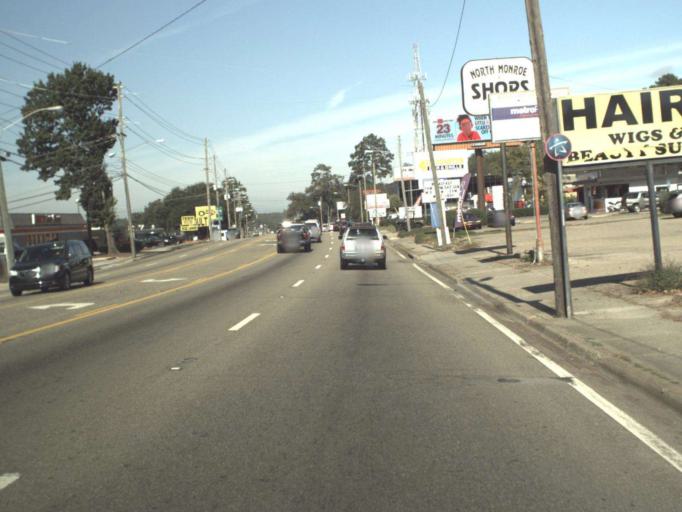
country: US
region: Florida
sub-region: Leon County
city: Tallahassee
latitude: 30.4678
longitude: -84.2855
